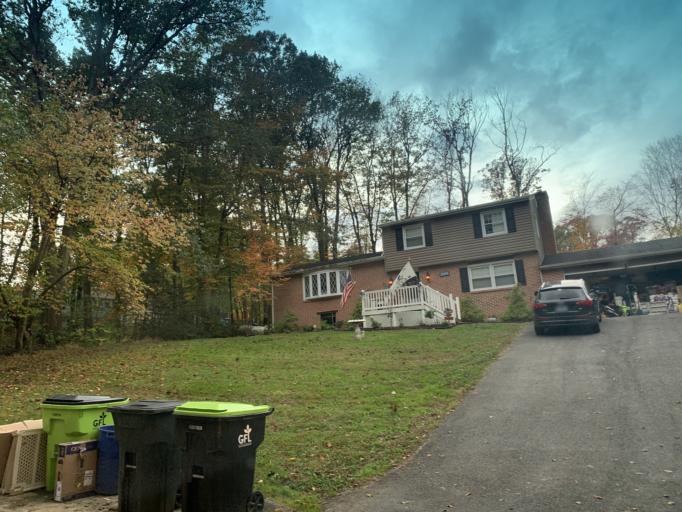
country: US
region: Maryland
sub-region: Harford County
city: South Bel Air
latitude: 39.5715
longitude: -76.3226
